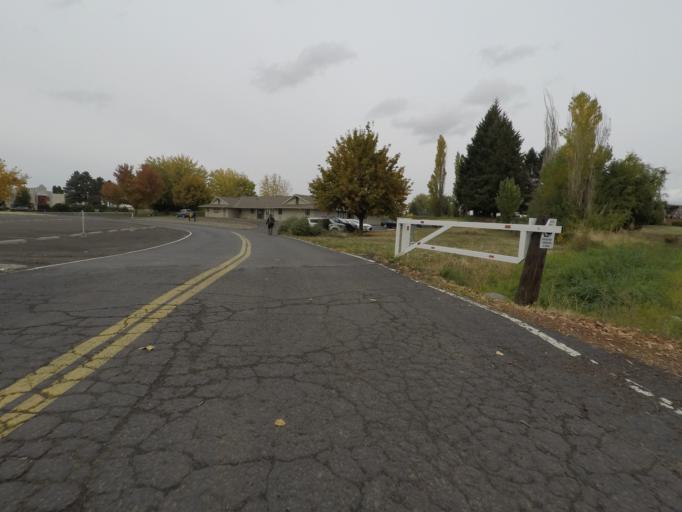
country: US
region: Washington
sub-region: Walla Walla County
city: Walla Walla East
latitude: 46.0796
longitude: -118.2736
